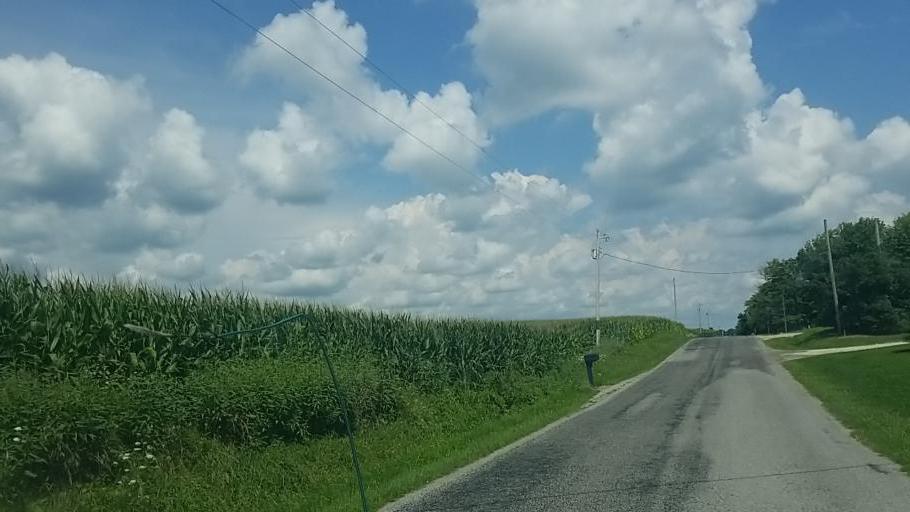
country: US
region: Ohio
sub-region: Wayne County
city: West Salem
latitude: 40.9973
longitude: -82.0784
